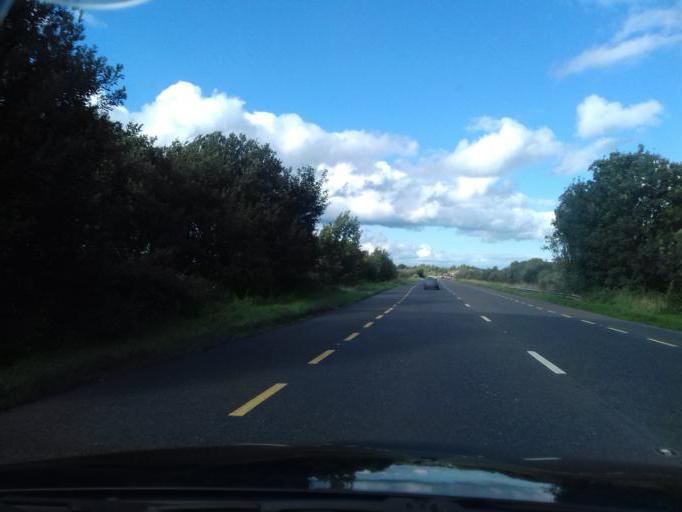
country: IE
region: Leinster
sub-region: An Iarmhi
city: Kilbeggan
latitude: 53.3470
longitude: -7.5011
